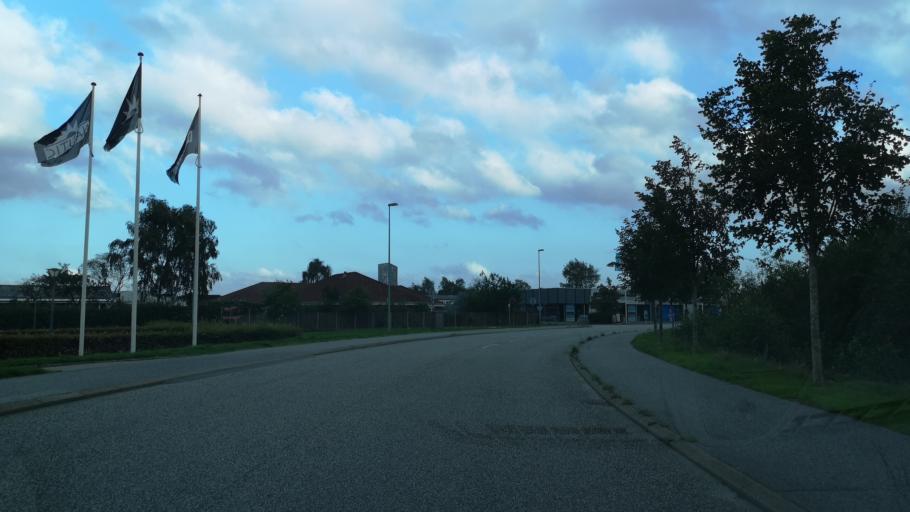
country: DK
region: Central Jutland
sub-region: Herning Kommune
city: Herning
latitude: 56.1361
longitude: 9.0068
